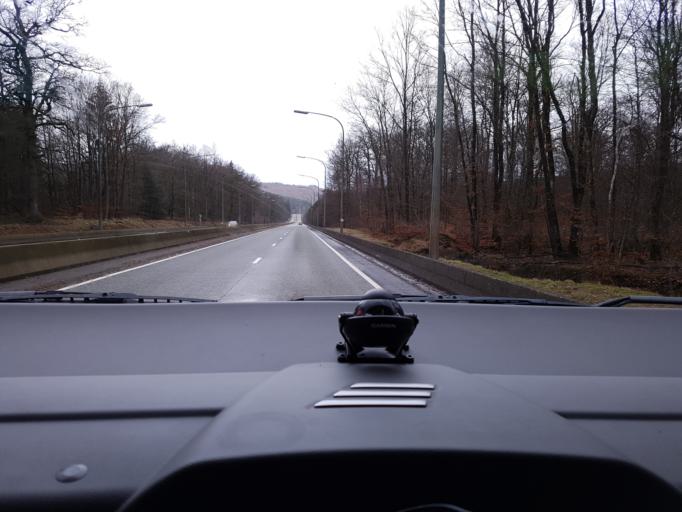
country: BE
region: Wallonia
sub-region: Province du Luxembourg
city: Tenneville
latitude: 50.1161
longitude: 5.4661
